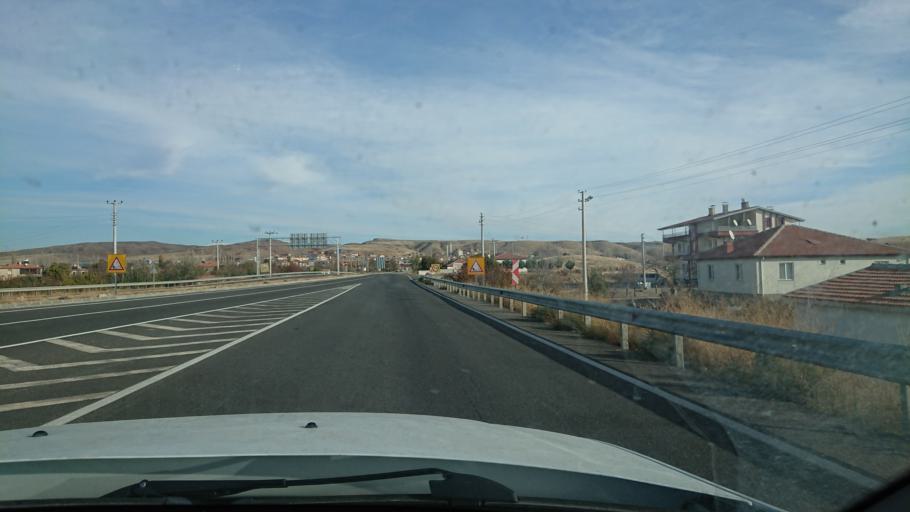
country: TR
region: Aksaray
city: Acipinar
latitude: 38.4783
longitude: 33.9008
